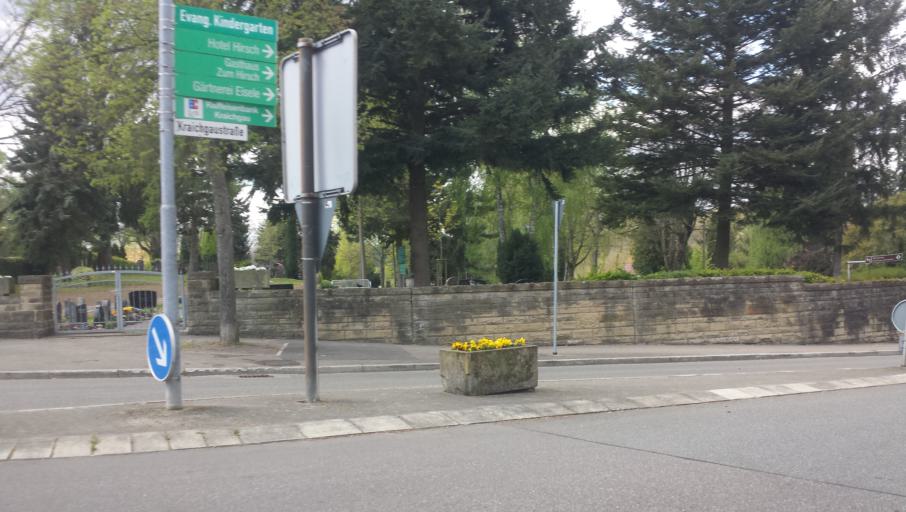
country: DE
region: Baden-Wuerttemberg
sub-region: Karlsruhe Region
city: Sinsheim
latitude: 49.1961
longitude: 8.8625
